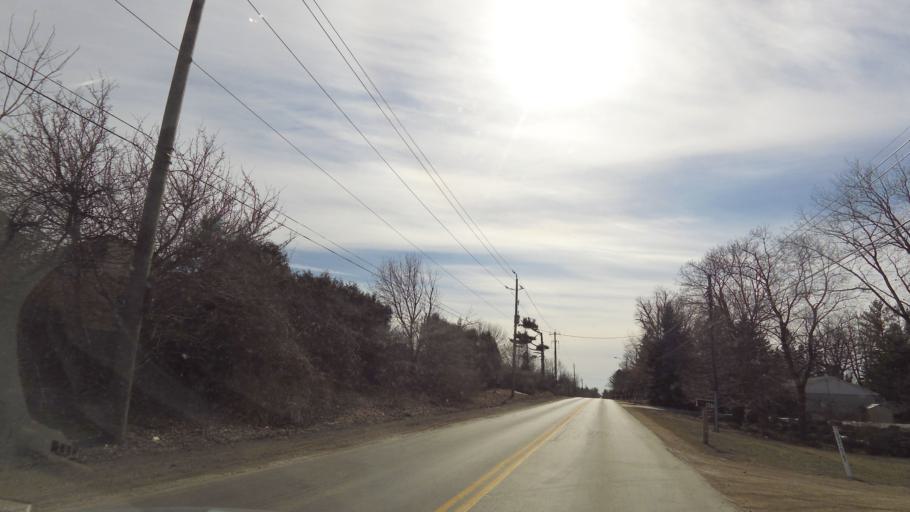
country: CA
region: Ontario
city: Burlington
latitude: 43.3488
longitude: -79.8887
